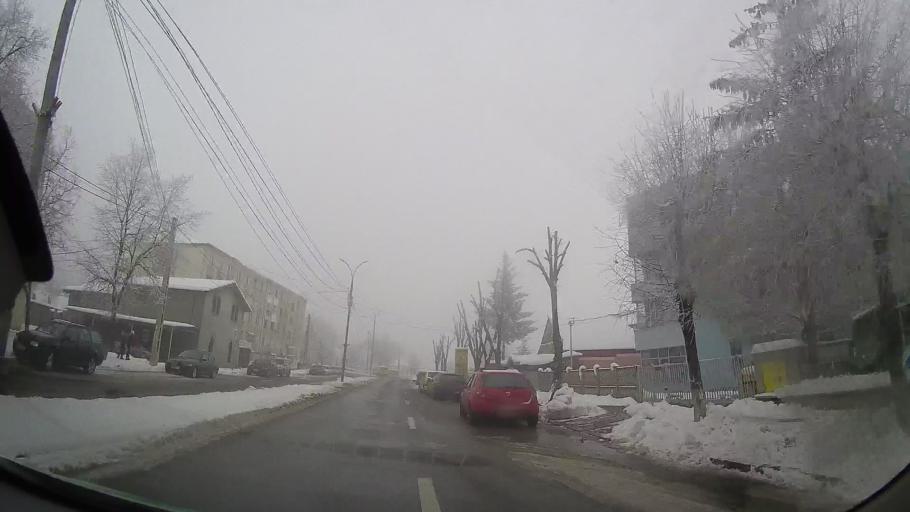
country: RO
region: Iasi
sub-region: Municipiul Pascani
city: Pascani
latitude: 47.2408
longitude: 26.7299
